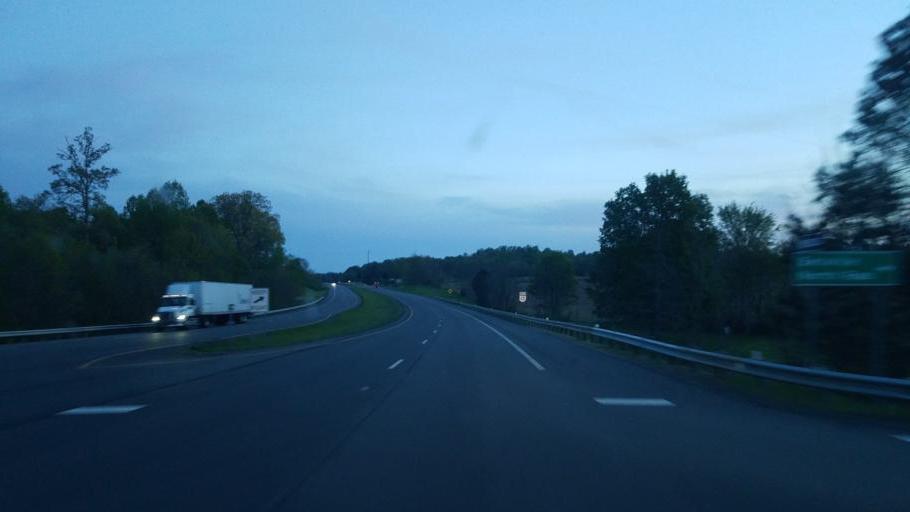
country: US
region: Ohio
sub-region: Sandusky County
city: Bellville
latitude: 40.6590
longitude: -82.5135
